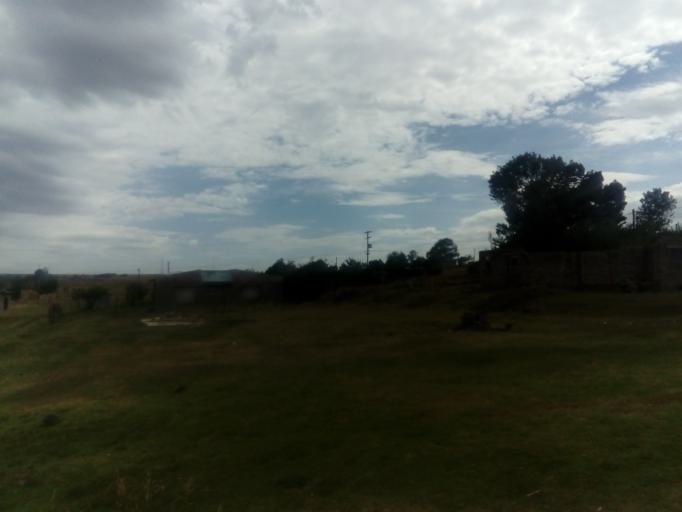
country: LS
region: Leribe
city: Maputsoe
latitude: -28.9380
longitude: 27.9448
